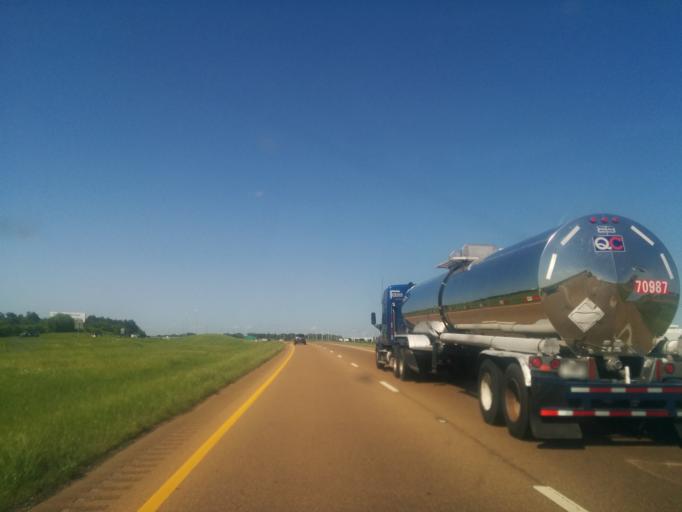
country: US
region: Mississippi
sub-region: Madison County
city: Canton
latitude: 32.5679
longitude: -90.0765
